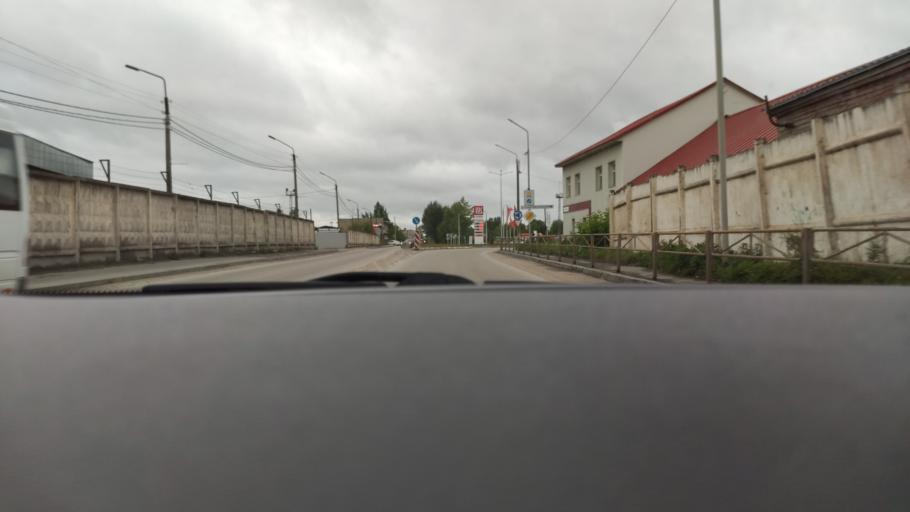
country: RU
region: Perm
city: Krasnokamsk
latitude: 58.0716
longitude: 55.7843
